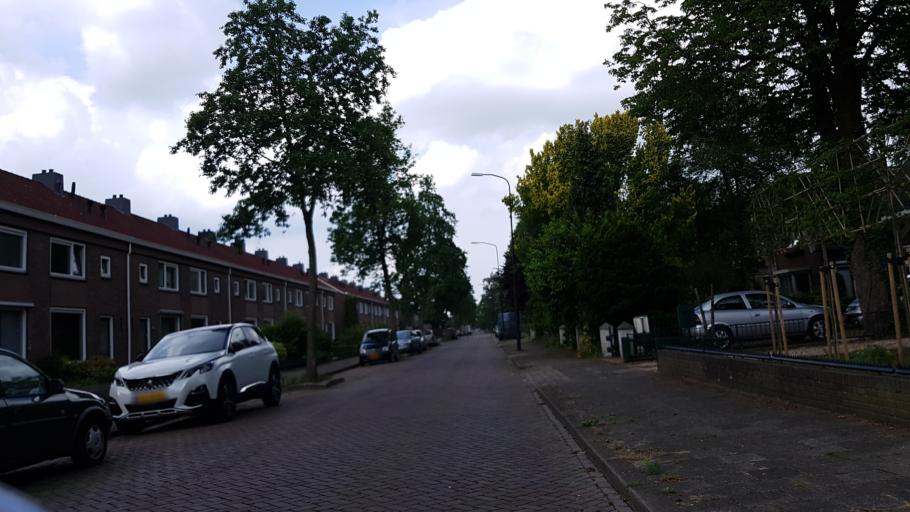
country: NL
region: Gelderland
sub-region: Gemeente Apeldoorn
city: Apeldoorn
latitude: 52.1892
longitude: 5.9701
